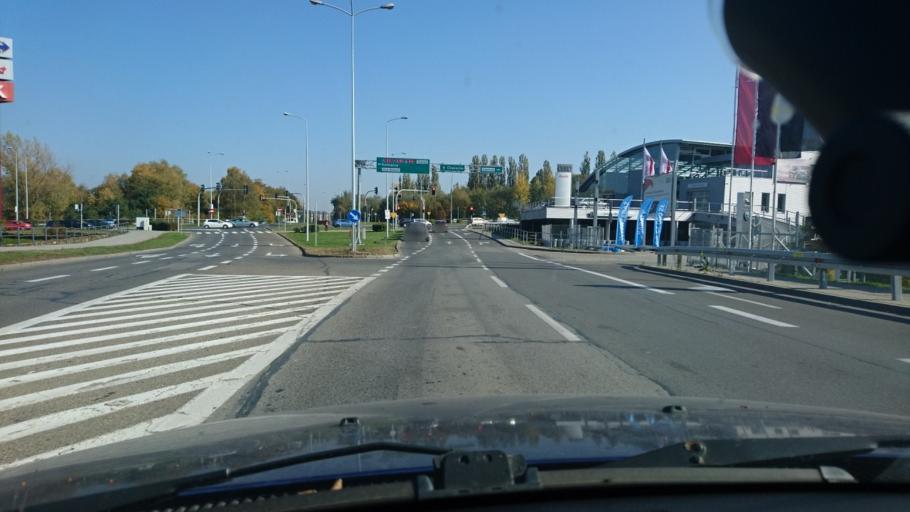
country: PL
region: Silesian Voivodeship
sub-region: Bielsko-Biala
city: Bielsko-Biala
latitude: 49.8391
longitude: 19.0366
